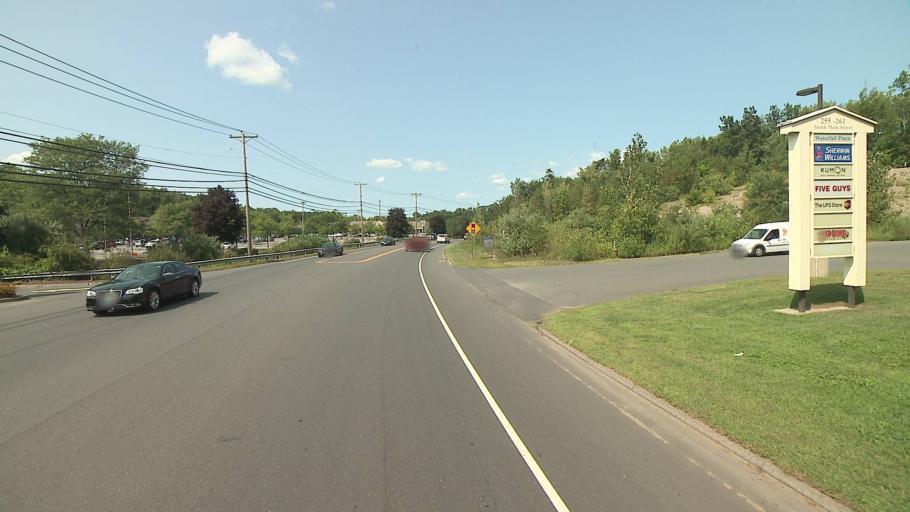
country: US
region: Connecticut
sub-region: Fairfield County
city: Newtown
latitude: 41.3713
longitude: -73.2718
